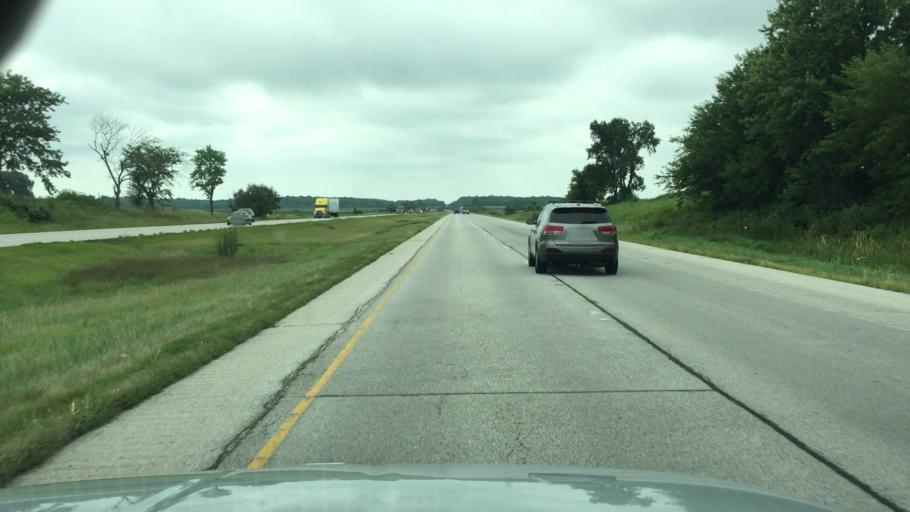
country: US
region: Illinois
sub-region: Knox County
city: Galesburg
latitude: 41.0895
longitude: -90.3336
